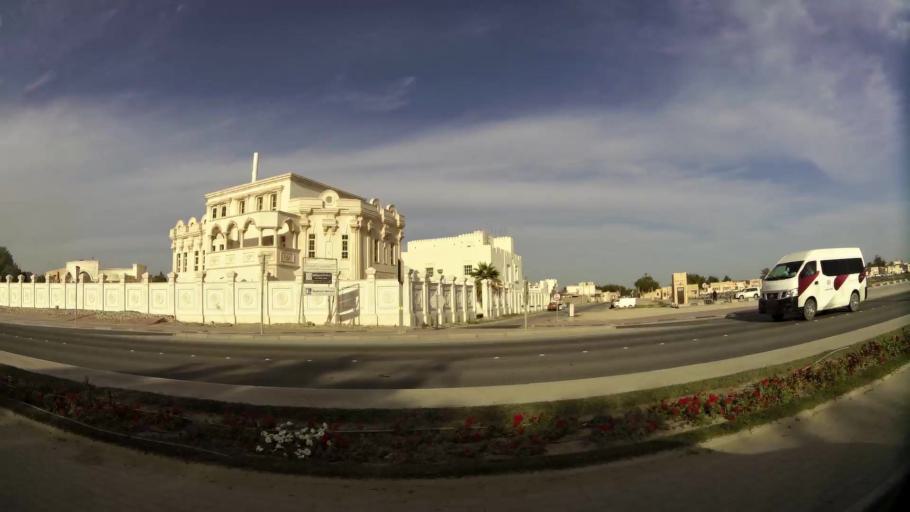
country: QA
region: Al Wakrah
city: Al Wakrah
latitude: 25.1739
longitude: 51.6065
